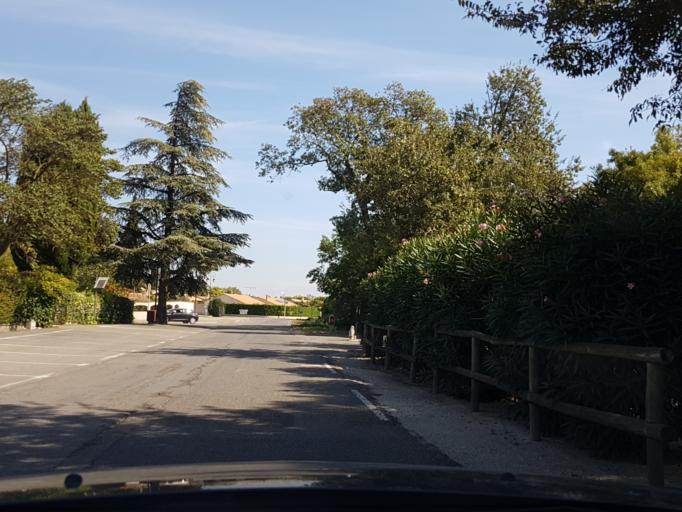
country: FR
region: Provence-Alpes-Cote d'Azur
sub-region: Departement des Bouches-du-Rhone
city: Noves
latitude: 43.8751
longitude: 4.9057
